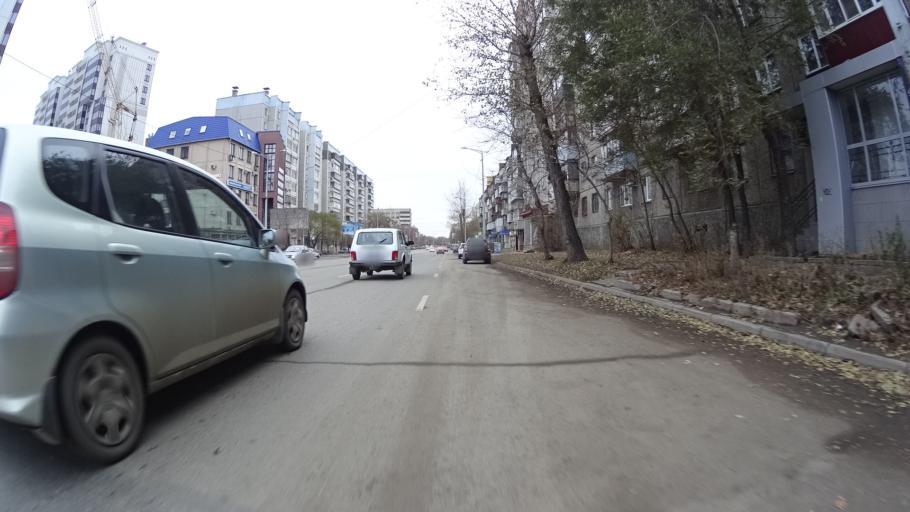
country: RU
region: Chelyabinsk
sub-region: Gorod Chelyabinsk
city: Chelyabinsk
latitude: 55.1574
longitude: 61.4170
